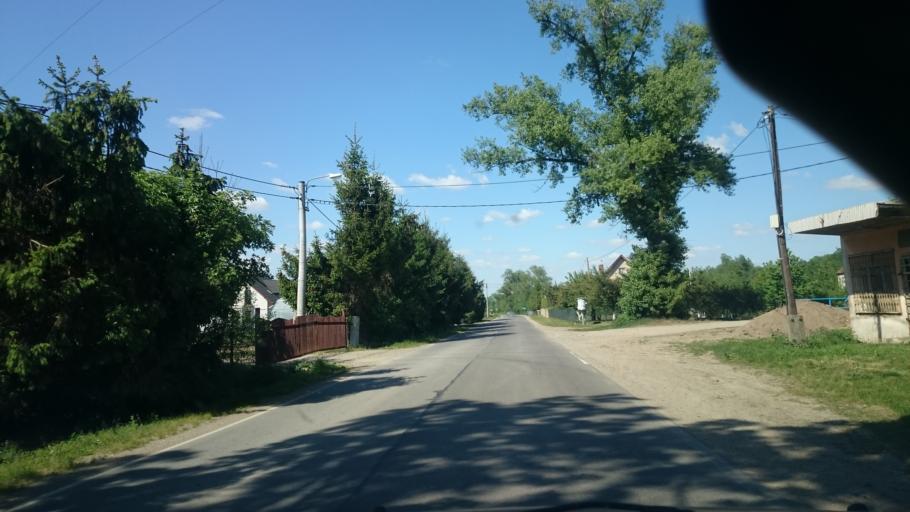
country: PL
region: Lower Silesian Voivodeship
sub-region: Powiat zabkowicki
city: Kamieniec Zabkowicki
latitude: 50.5002
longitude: 16.8319
